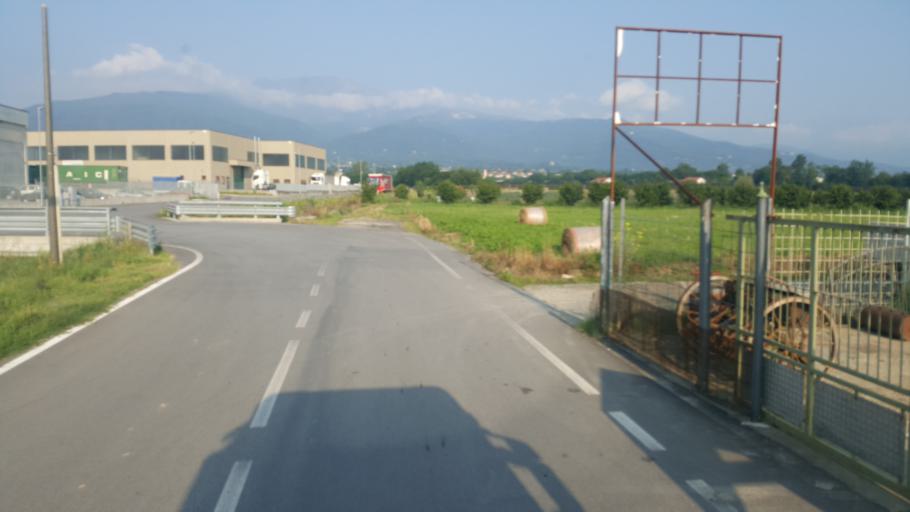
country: IT
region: Piedmont
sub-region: Provincia di Cuneo
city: Barge
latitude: 44.7365
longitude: 7.3599
